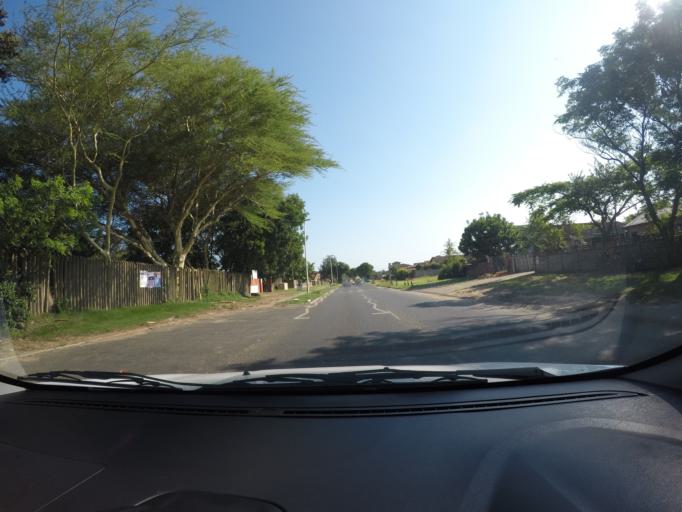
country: ZA
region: KwaZulu-Natal
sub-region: uThungulu District Municipality
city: Richards Bay
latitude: -28.7274
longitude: 32.0419
